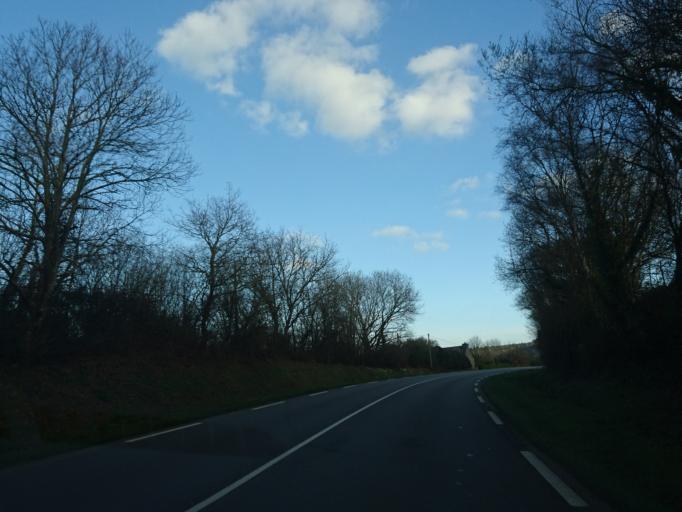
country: FR
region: Brittany
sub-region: Departement du Finistere
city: Hopital-Camfrout
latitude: 48.2828
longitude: -4.2488
